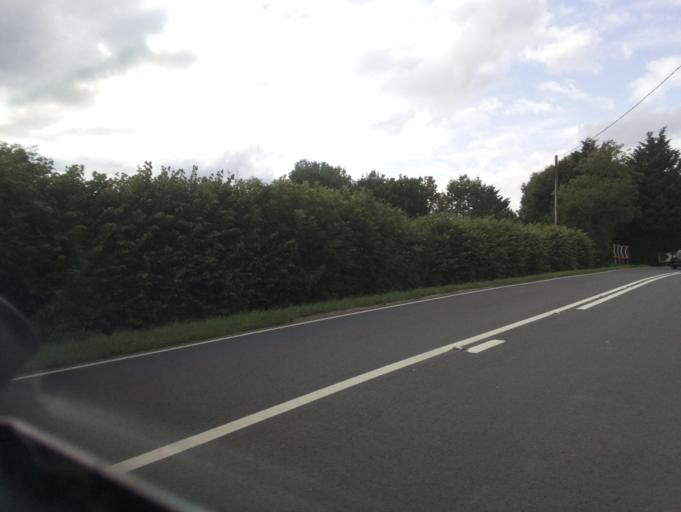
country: GB
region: England
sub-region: Warwickshire
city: Dunchurch
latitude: 52.3172
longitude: -1.3155
